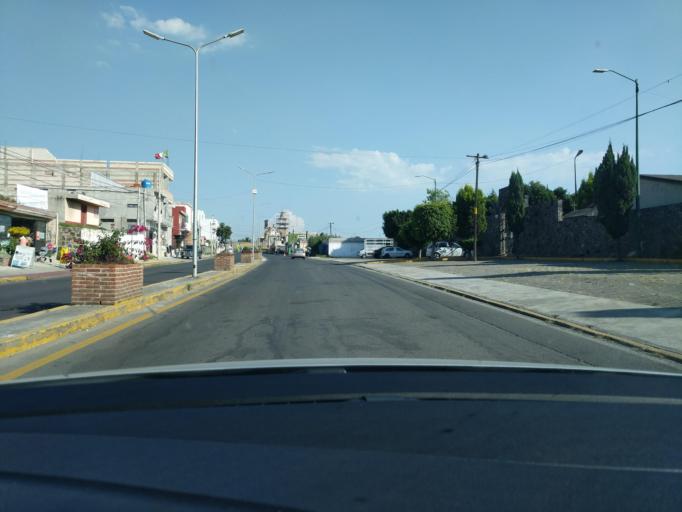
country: MX
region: Puebla
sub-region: San Gregorio Atzompa
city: Chipilo de Francisco Javier Mina
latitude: 19.0239
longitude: -98.3113
